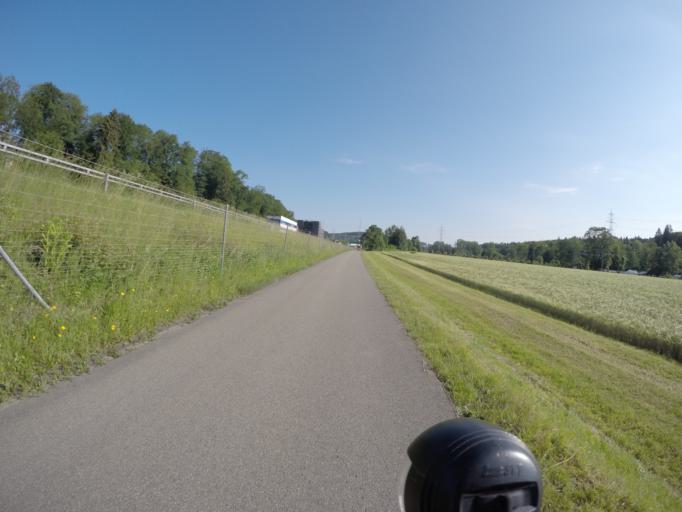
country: CH
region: Zurich
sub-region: Bezirk Winterthur
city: Toss
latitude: 47.4730
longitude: 8.7053
